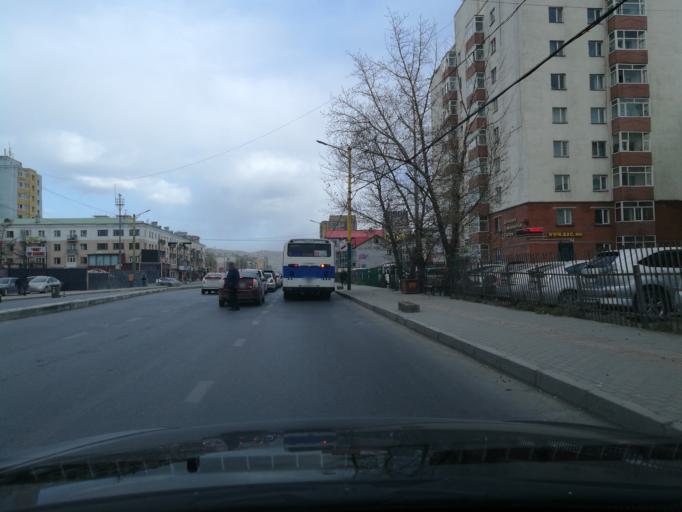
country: MN
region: Ulaanbaatar
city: Ulaanbaatar
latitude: 47.9289
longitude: 106.9157
